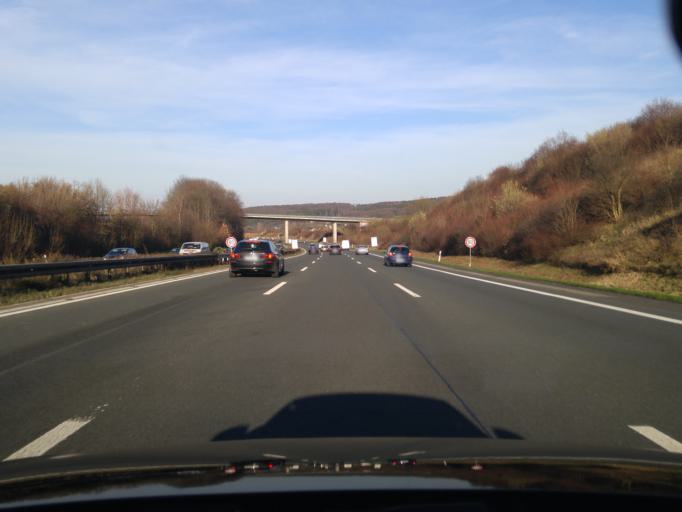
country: DE
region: North Rhine-Westphalia
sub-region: Regierungsbezirk Koln
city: Stossdorf
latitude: 50.7377
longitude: 7.2387
